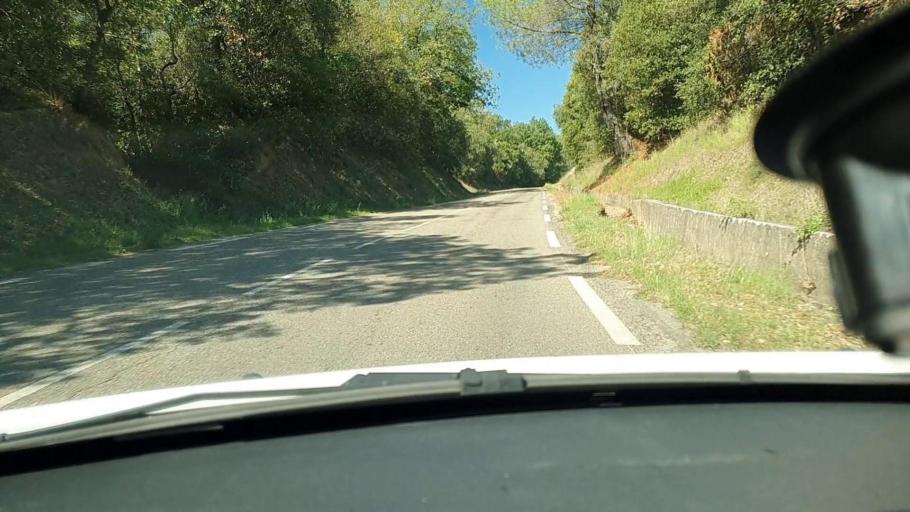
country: FR
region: Languedoc-Roussillon
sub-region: Departement du Gard
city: Saint-Paulet-de-Caisson
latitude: 44.2445
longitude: 4.5869
